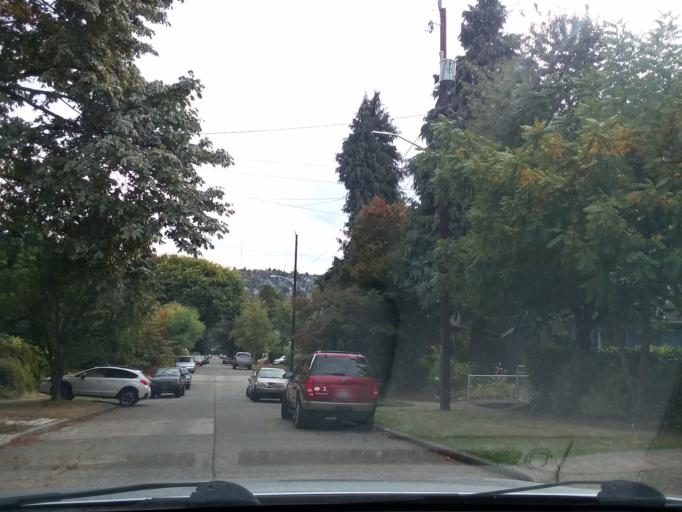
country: US
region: Washington
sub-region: King County
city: Seattle
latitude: 47.6571
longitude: -122.3526
